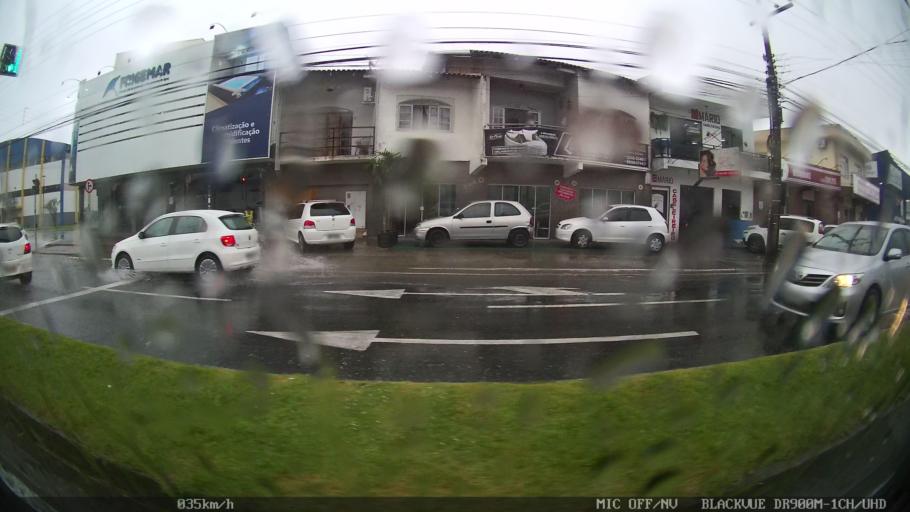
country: BR
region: Santa Catarina
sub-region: Itajai
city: Itajai
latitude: -26.9289
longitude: -48.6456
